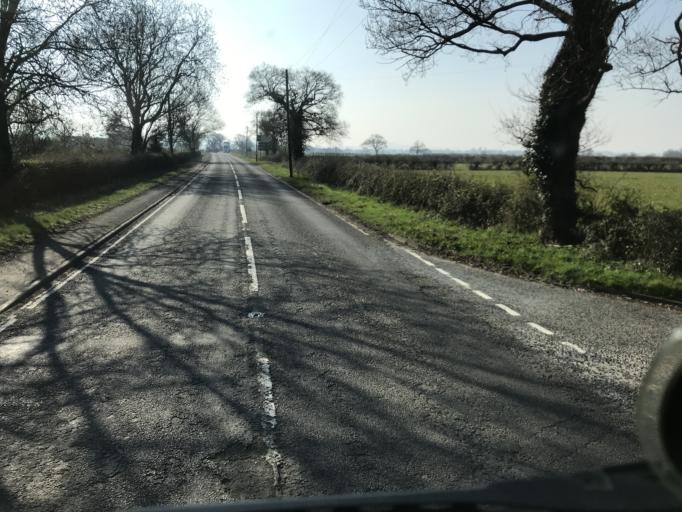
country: GB
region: England
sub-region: Cheshire West and Chester
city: Waverton
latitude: 53.1407
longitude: -2.8109
